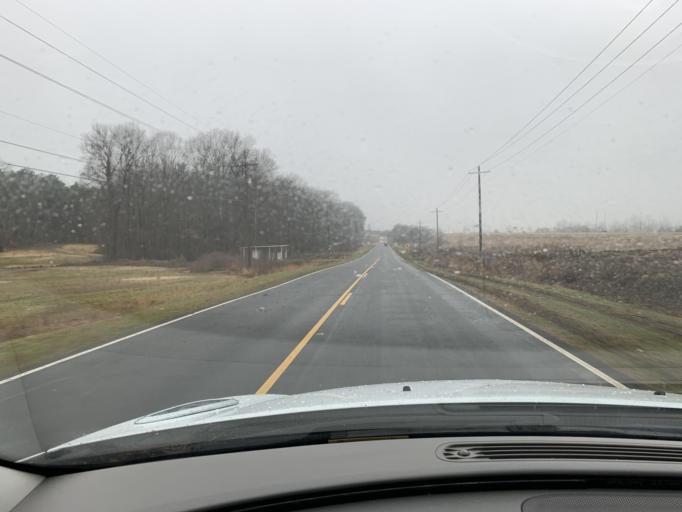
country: US
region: Mississippi
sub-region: De Soto County
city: Hernando
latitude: 34.8605
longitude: -89.9770
